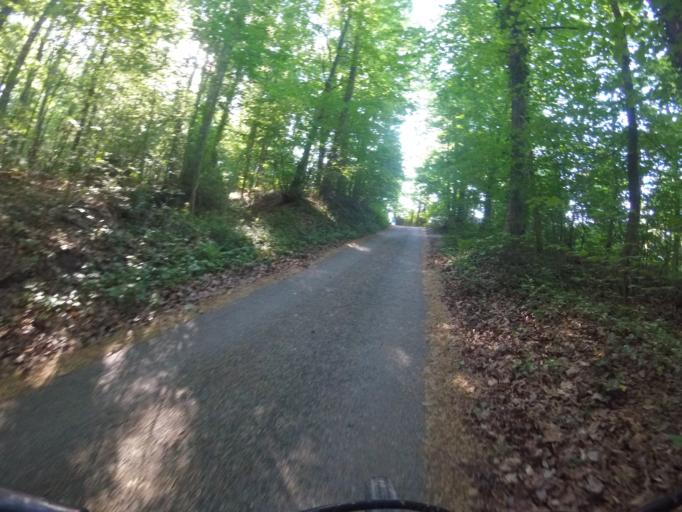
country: DE
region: Baden-Wuerttemberg
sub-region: Regierungsbezirk Stuttgart
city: Aspach
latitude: 48.9836
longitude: 9.4184
